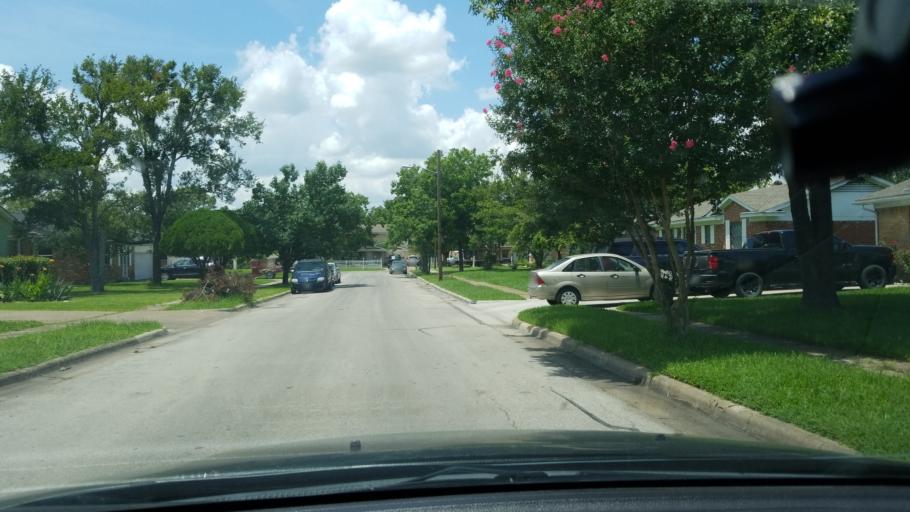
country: US
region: Texas
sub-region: Dallas County
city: Balch Springs
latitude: 32.7391
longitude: -96.6511
